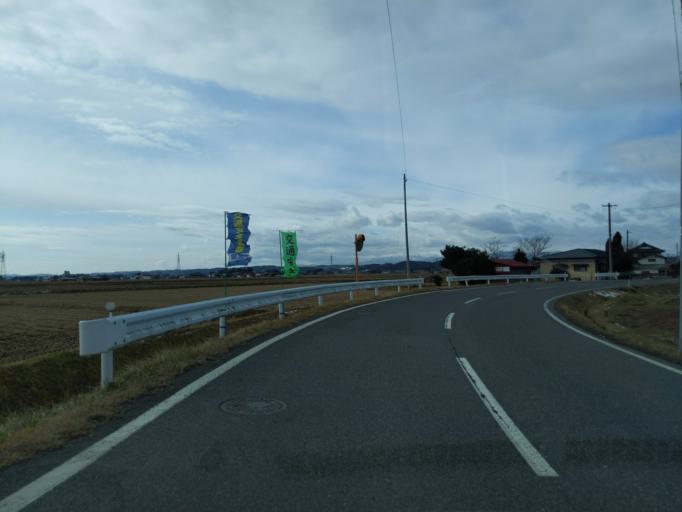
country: JP
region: Iwate
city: Mizusawa
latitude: 39.0871
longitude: 141.1633
